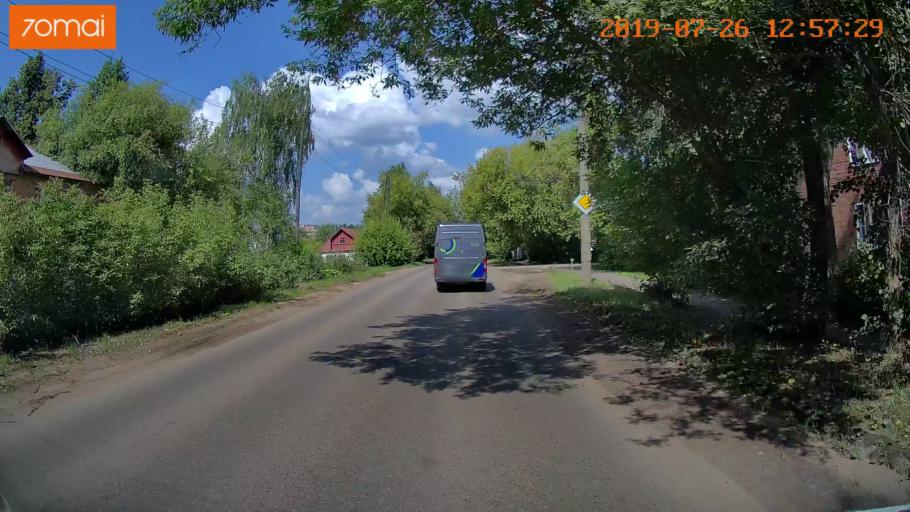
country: RU
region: Ivanovo
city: Bogorodskoye
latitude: 57.0195
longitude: 41.0208
